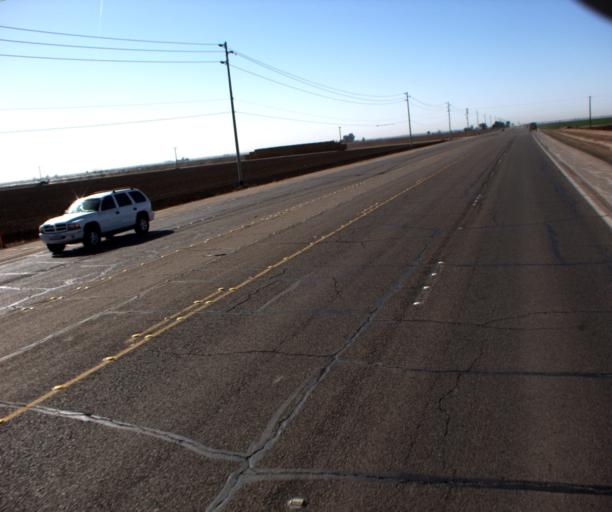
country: US
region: Arizona
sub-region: Yuma County
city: Somerton
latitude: 32.5840
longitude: -114.7699
